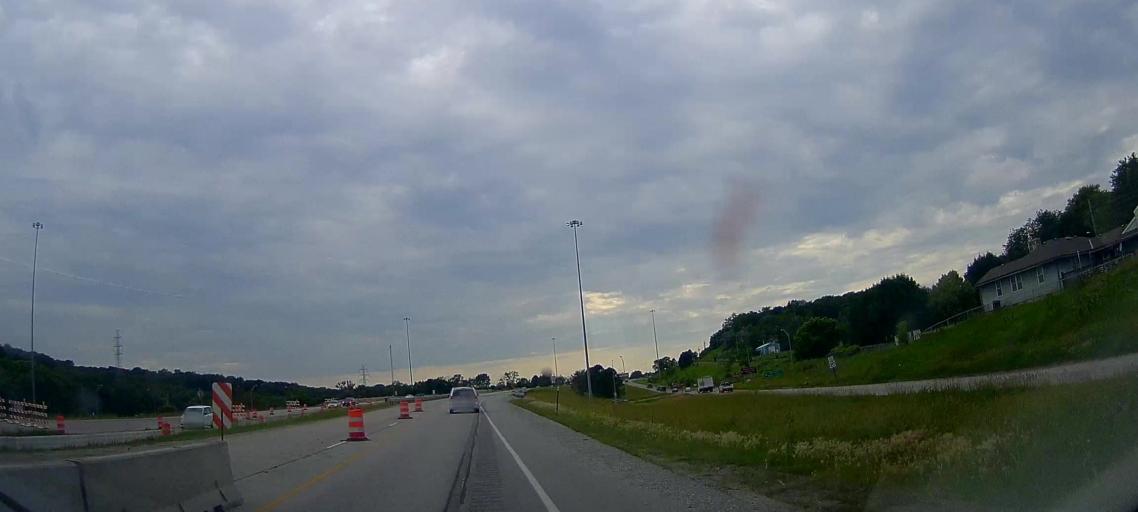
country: US
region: Iowa
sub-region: Pottawattamie County
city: Carter Lake
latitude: 41.3449
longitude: -95.9624
